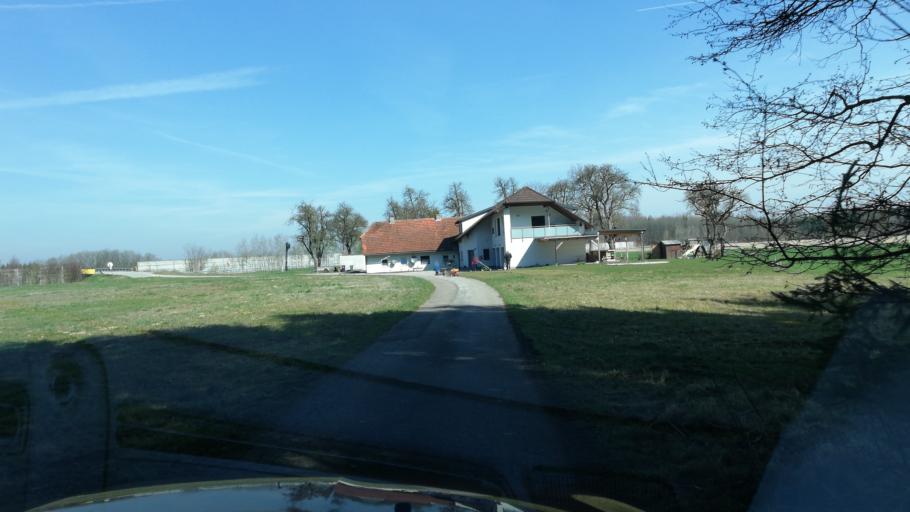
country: AT
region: Upper Austria
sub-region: Wels-Land
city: Sattledt
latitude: 48.0971
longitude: 14.0826
